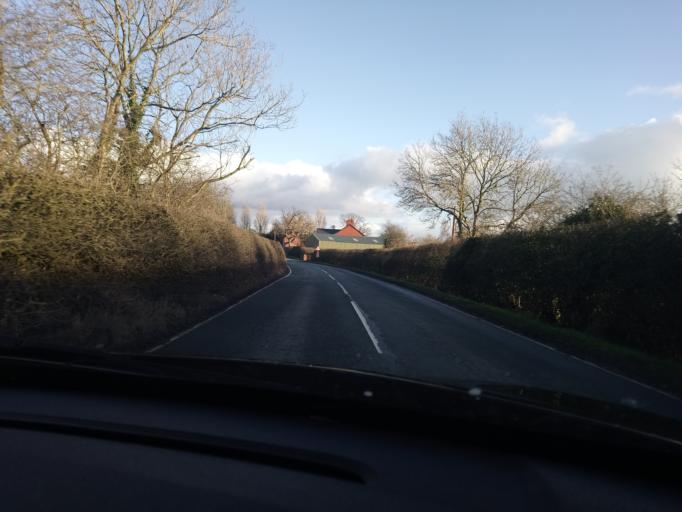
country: GB
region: England
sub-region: Shropshire
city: Ellesmere
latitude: 52.9175
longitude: -2.9186
